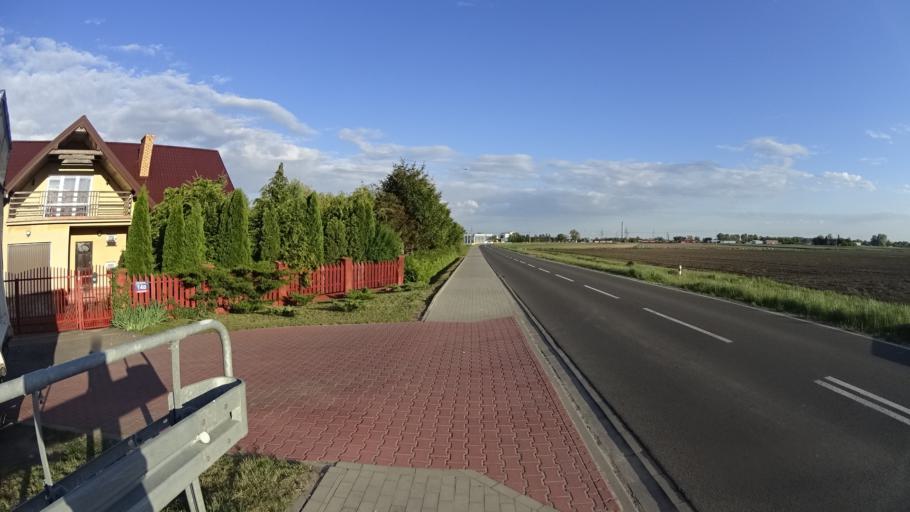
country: PL
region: Masovian Voivodeship
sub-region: Powiat warszawski zachodni
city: Jozefow
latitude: 52.2218
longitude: 20.7385
